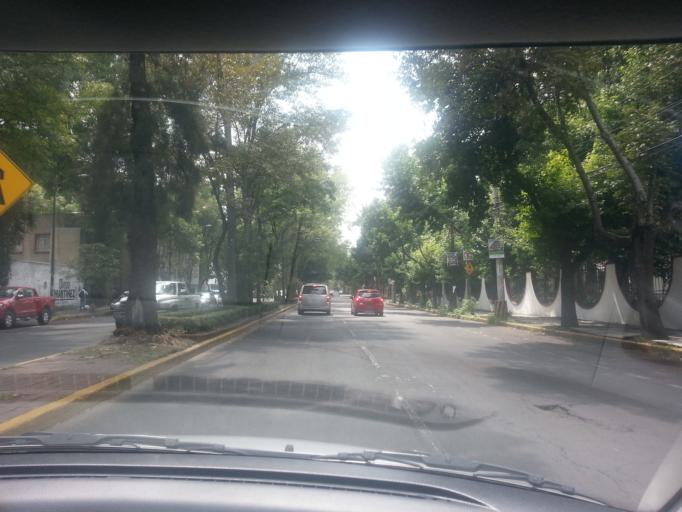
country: MX
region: Mexico City
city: Coyoacan
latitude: 19.3511
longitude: -99.1725
